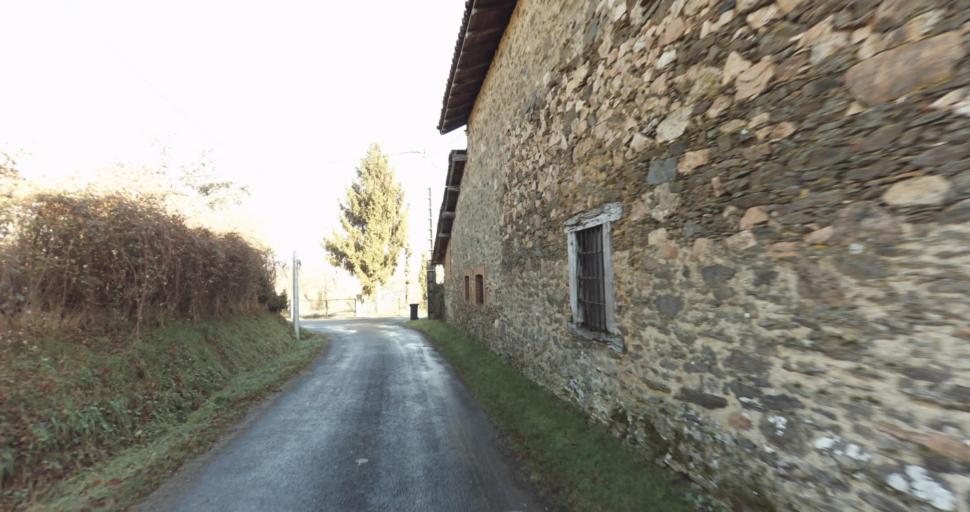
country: FR
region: Limousin
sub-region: Departement de la Haute-Vienne
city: Aixe-sur-Vienne
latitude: 45.7826
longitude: 1.1291
